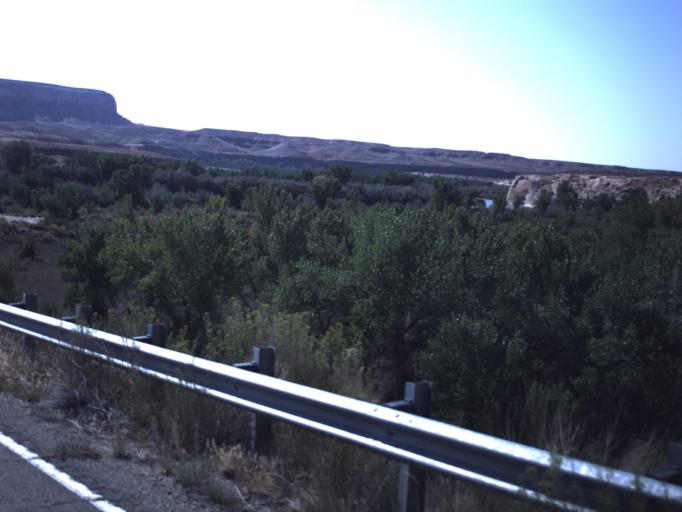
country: US
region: Utah
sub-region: San Juan County
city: Blanding
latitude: 37.2598
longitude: -109.6210
